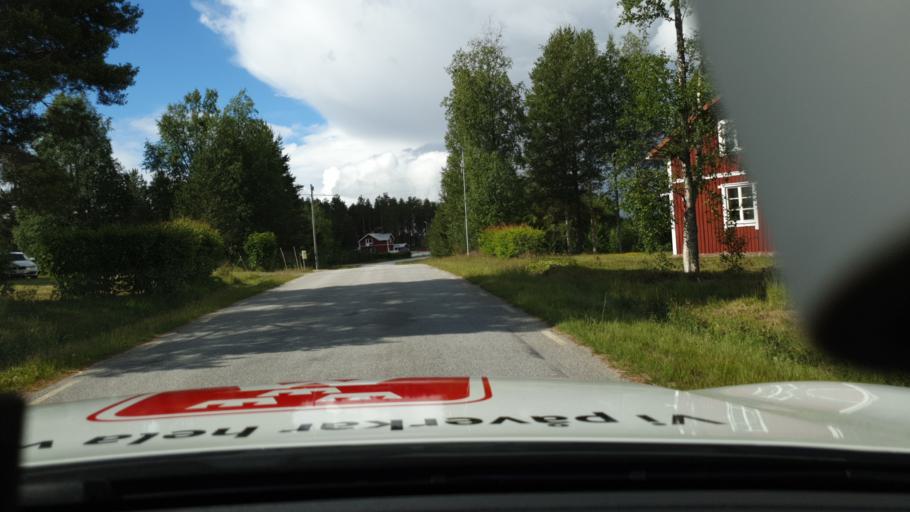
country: SE
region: Norrbotten
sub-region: Pitea Kommun
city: Rosvik
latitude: 65.3905
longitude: 21.7320
